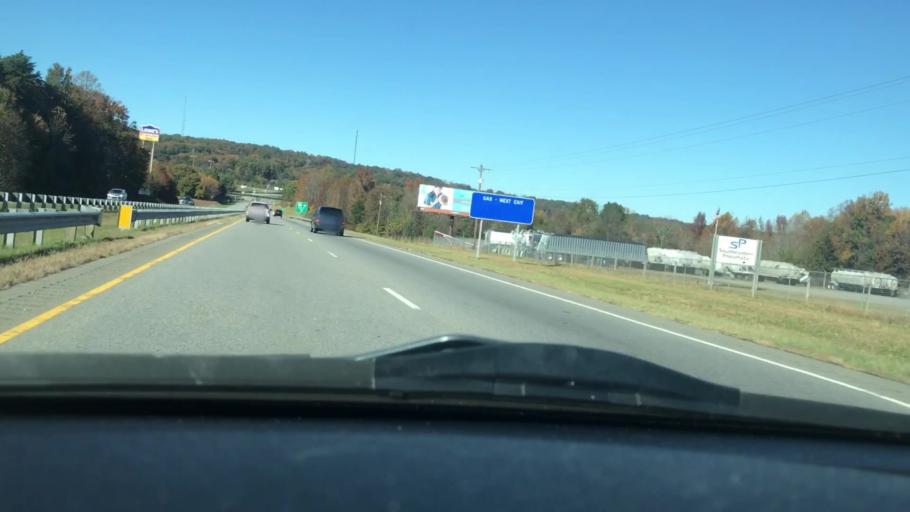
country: US
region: North Carolina
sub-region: Rockingham County
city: Mayodan
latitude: 36.4098
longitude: -79.9377
